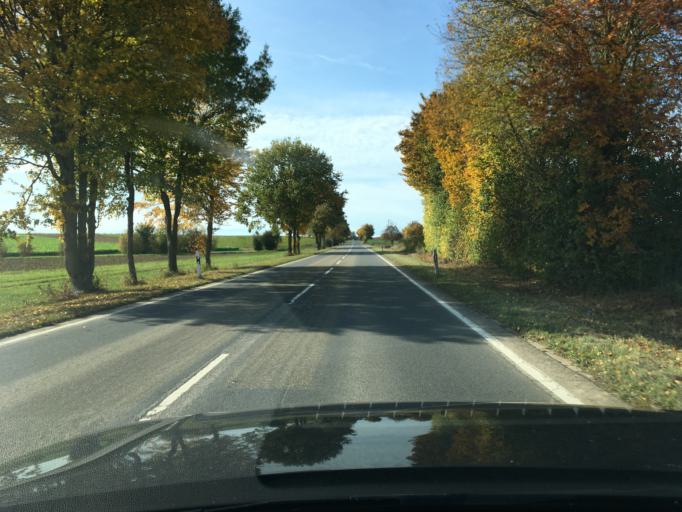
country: DE
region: Baden-Wuerttemberg
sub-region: Regierungsbezirk Stuttgart
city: Bad Rappenau
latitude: 49.2337
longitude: 9.0720
